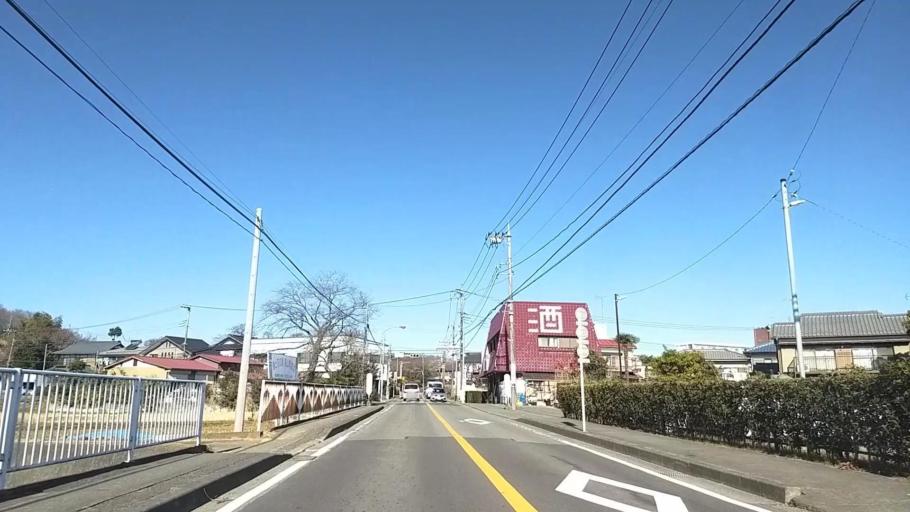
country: JP
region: Tokyo
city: Hachioji
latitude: 35.6052
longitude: 139.2986
